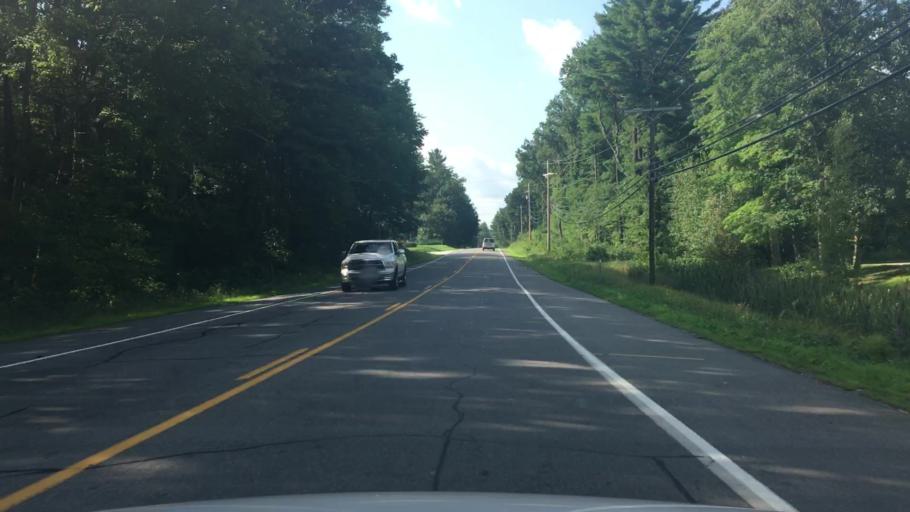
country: US
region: New Hampshire
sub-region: Rockingham County
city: Auburn
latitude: 42.9567
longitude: -71.3563
